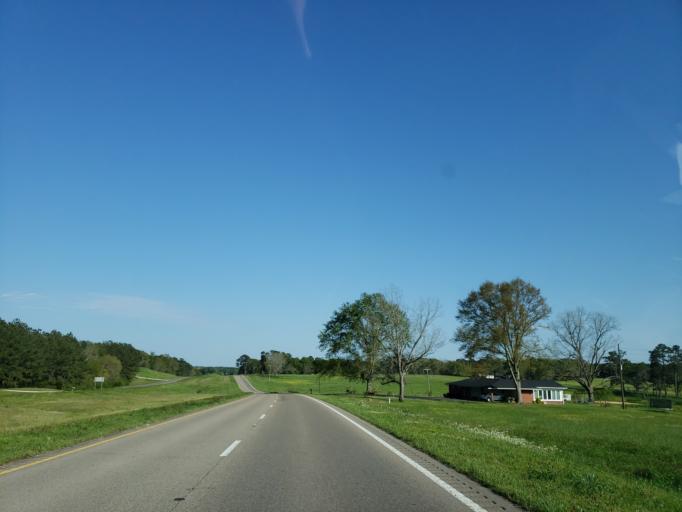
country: US
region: Mississippi
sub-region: Jones County
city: Ellisville
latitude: 31.6889
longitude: -89.3285
